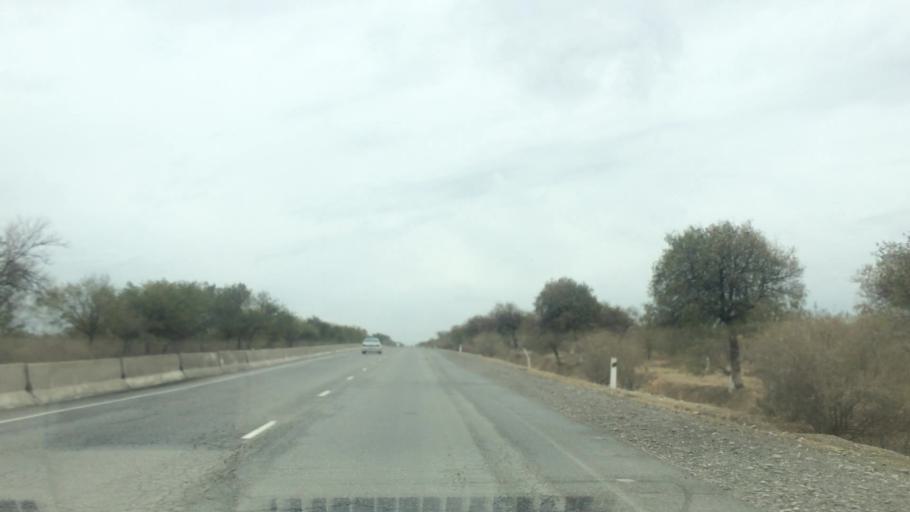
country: UZ
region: Samarqand
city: Bulung'ur
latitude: 39.8212
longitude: 67.3906
